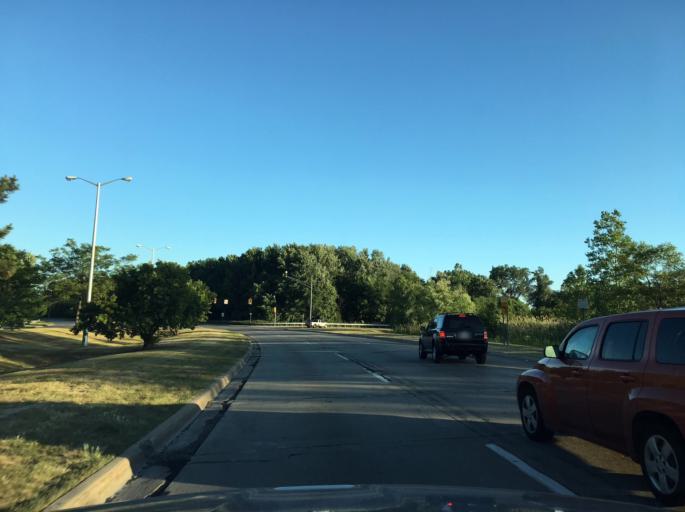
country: US
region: Michigan
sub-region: Macomb County
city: Sterling Heights
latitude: 42.5836
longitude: -82.9933
